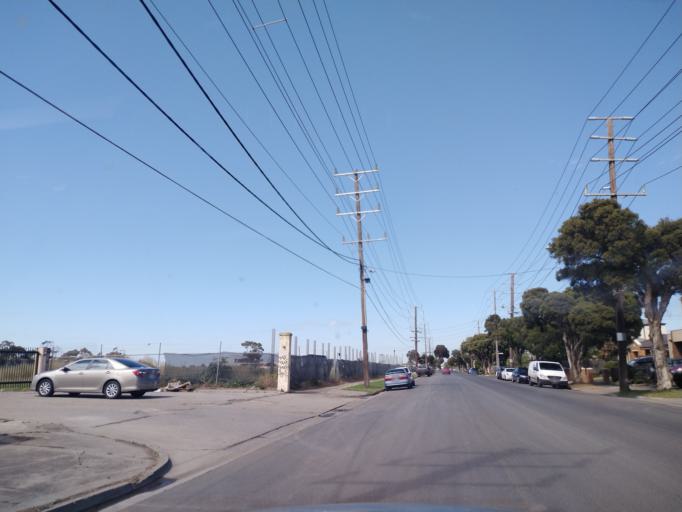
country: AU
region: Victoria
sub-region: Hobsons Bay
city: Altona North
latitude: -37.8271
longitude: 144.8572
